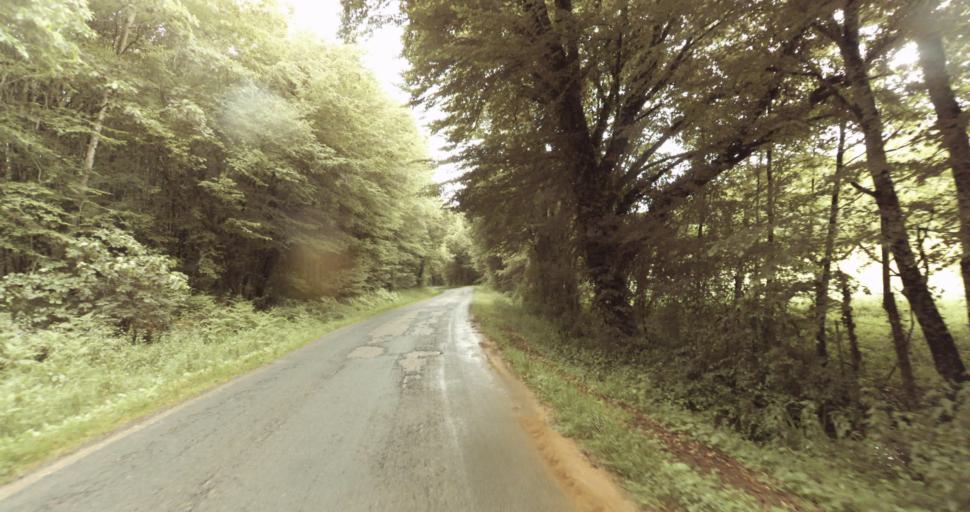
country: FR
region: Aquitaine
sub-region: Departement de la Dordogne
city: Belves
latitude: 44.7525
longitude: 0.9429
